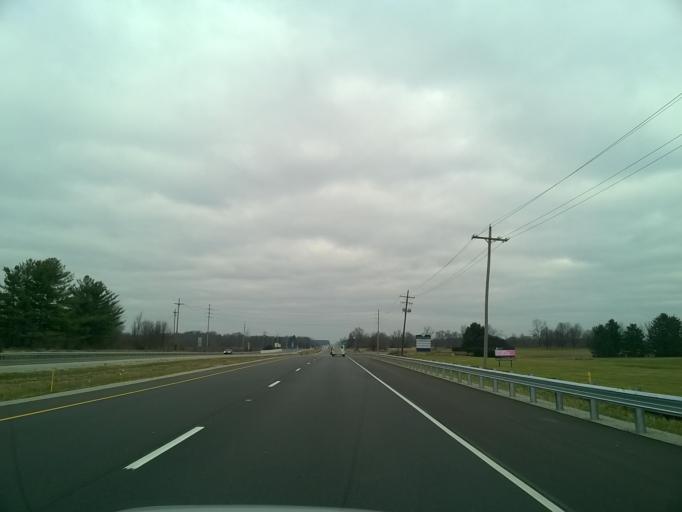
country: US
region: Indiana
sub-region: Hamilton County
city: Westfield
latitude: 40.0757
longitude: -86.1277
